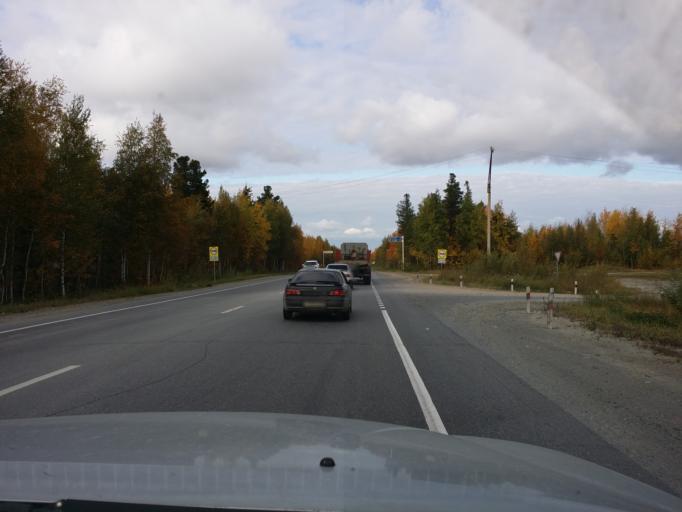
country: RU
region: Khanty-Mansiyskiy Avtonomnyy Okrug
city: Megion
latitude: 61.0575
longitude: 76.2968
